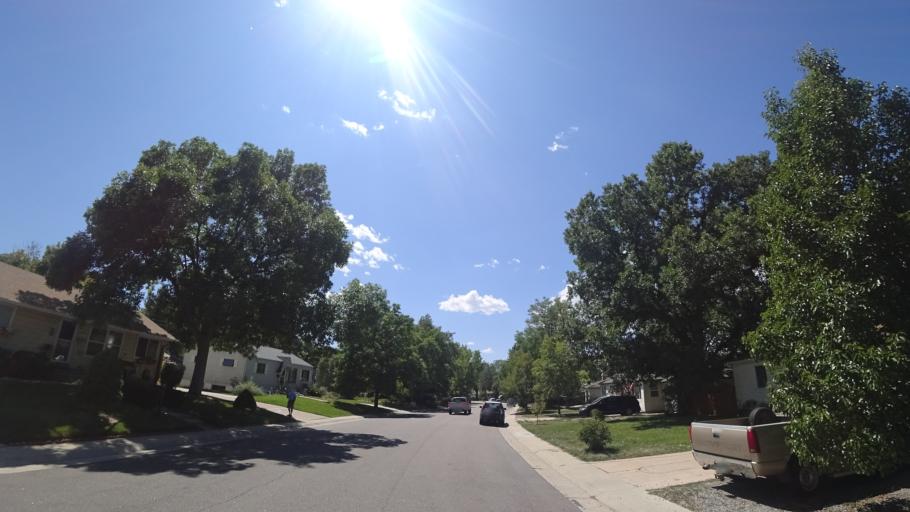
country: US
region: Colorado
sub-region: Arapahoe County
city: Littleton
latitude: 39.6121
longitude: -104.9965
